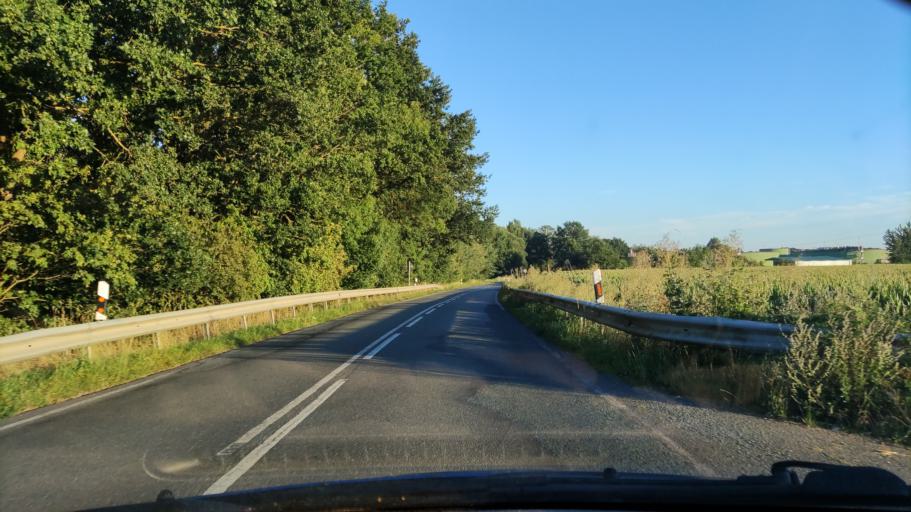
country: DE
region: Lower Saxony
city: Luechow
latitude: 52.9874
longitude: 11.1565
